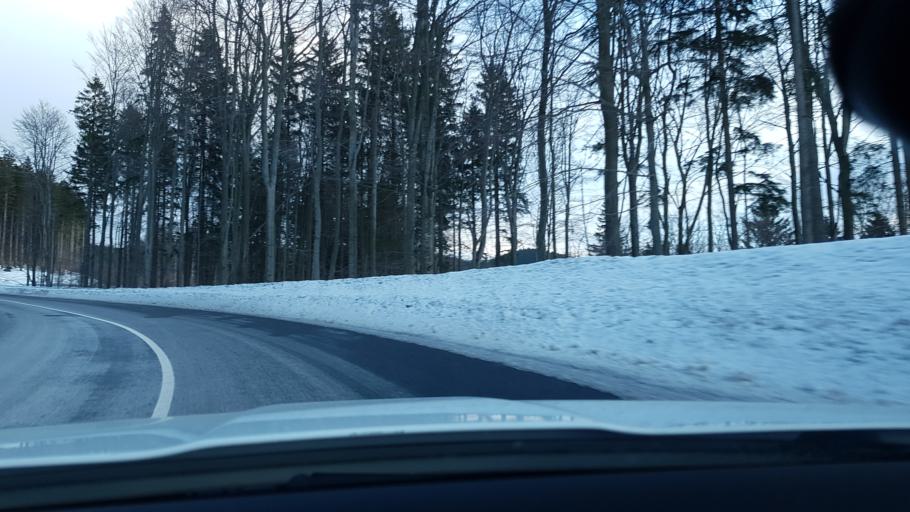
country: CZ
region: Olomoucky
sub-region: Okres Sumperk
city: Loucna nad Desnou
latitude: 50.1127
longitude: 17.1443
